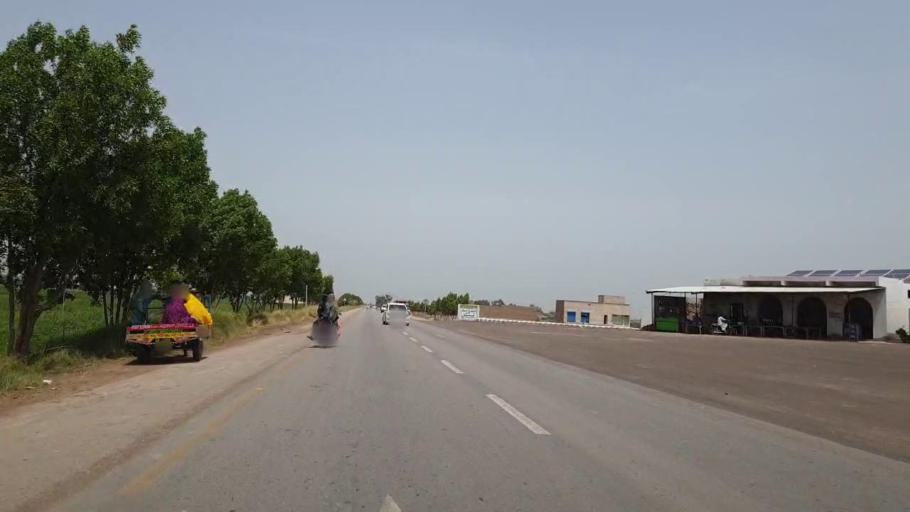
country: PK
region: Sindh
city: Nawabshah
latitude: 26.2237
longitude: 68.4955
